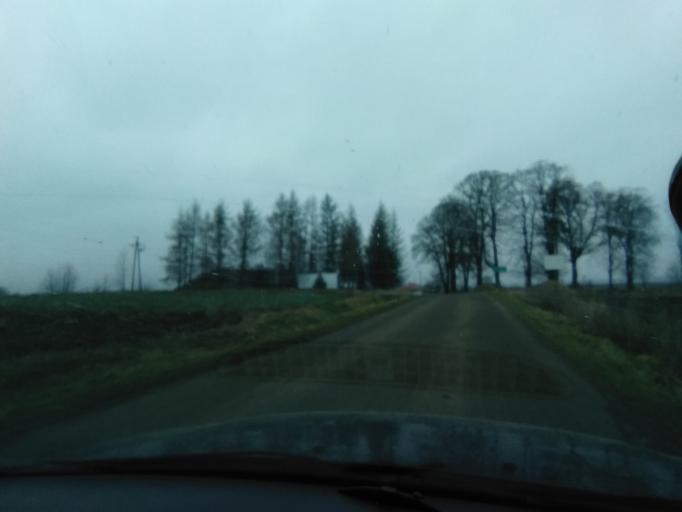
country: PL
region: Subcarpathian Voivodeship
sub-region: Powiat jaroslawski
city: Pruchnik
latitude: 49.9194
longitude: 22.5346
